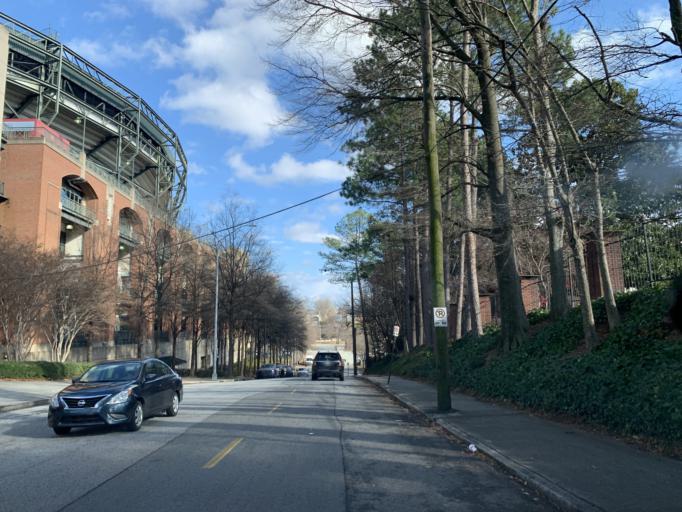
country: US
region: Georgia
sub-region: Fulton County
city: Atlanta
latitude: 33.7343
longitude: -84.3908
